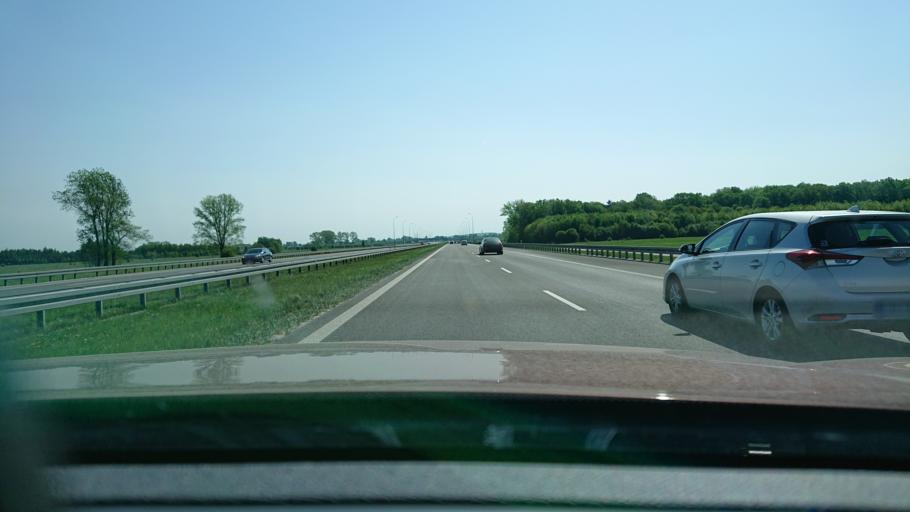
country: PL
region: Subcarpathian Voivodeship
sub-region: Powiat lancucki
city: Czarna
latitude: 50.0922
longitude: 22.1502
